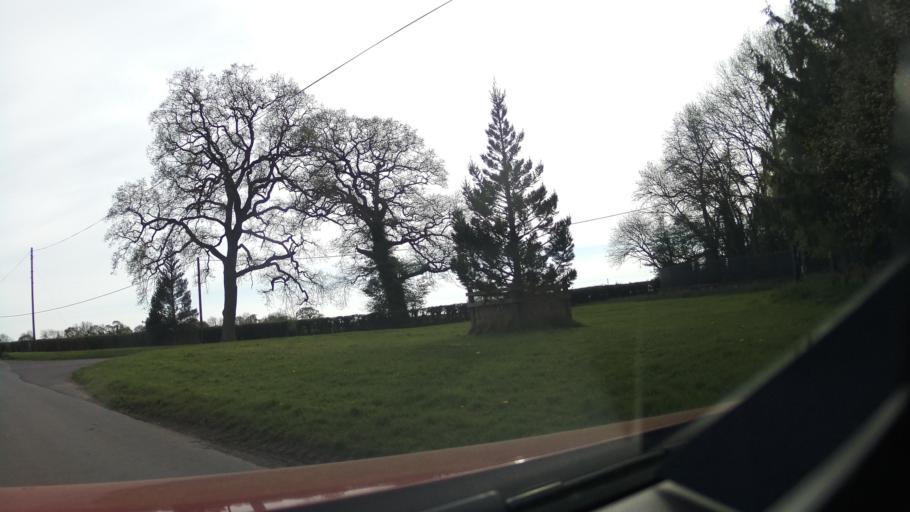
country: GB
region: England
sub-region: Somerset
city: Milborne Port
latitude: 50.9414
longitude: -2.4707
